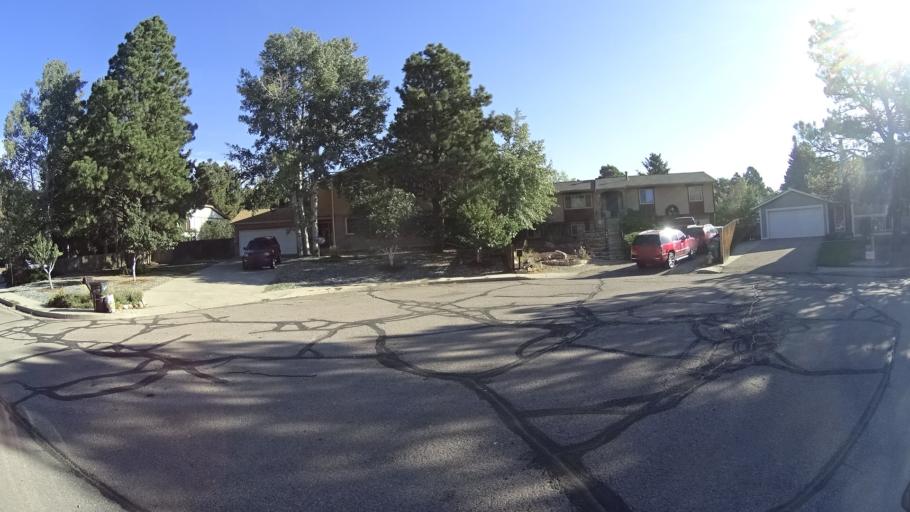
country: US
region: Colorado
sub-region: El Paso County
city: Cimarron Hills
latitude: 38.9069
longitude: -104.7556
